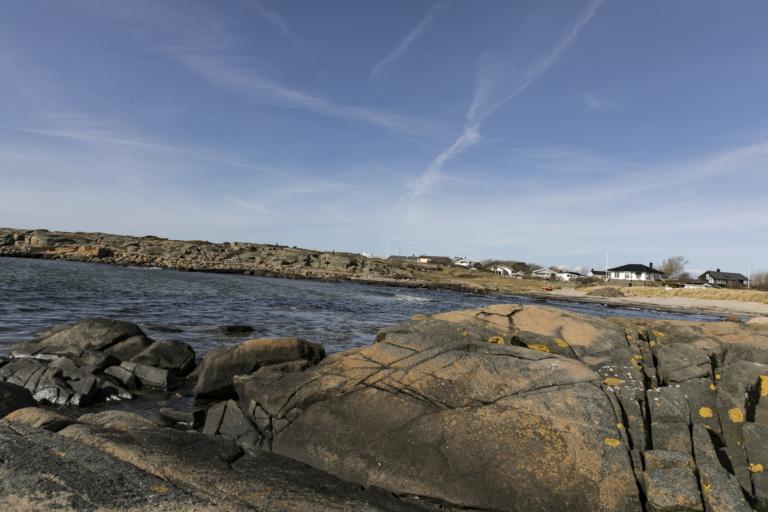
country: SE
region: Halland
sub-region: Varbergs Kommun
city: Varberg
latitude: 57.1139
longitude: 12.2120
